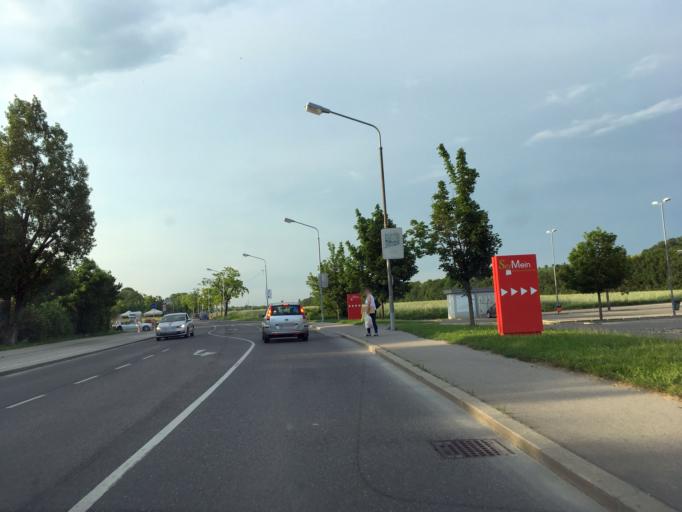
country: AT
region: Lower Austria
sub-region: Politischer Bezirk Wien-Umgebung
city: Gerasdorf bei Wien
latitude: 48.2674
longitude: 16.4563
